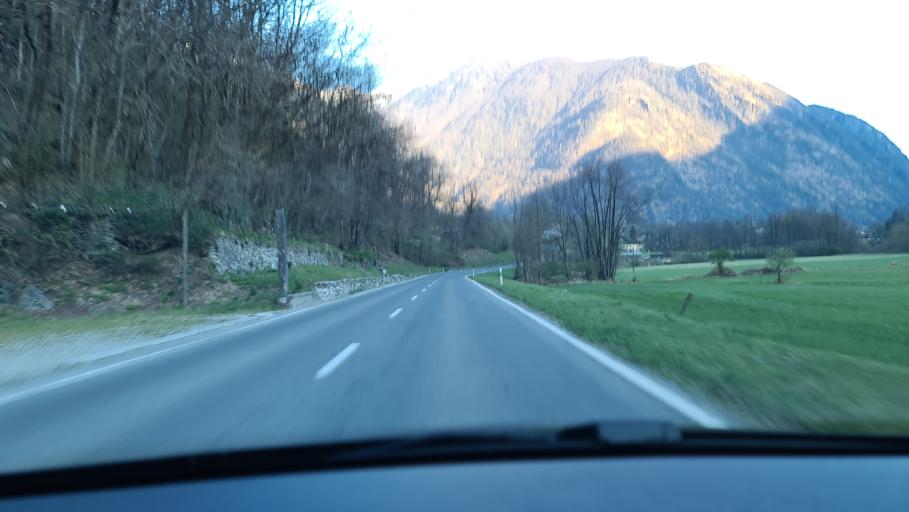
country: CH
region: Ticino
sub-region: Locarno District
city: Verscio
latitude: 46.2317
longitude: 8.7340
